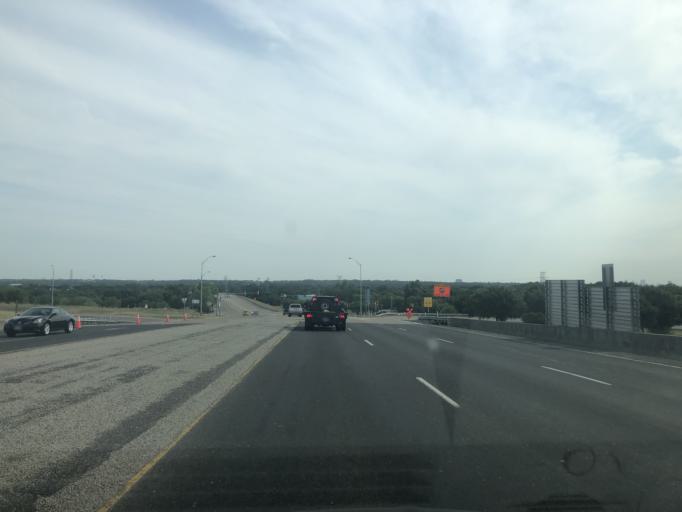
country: US
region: Texas
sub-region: Tarrant County
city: Benbrook
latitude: 32.6844
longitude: -97.4595
